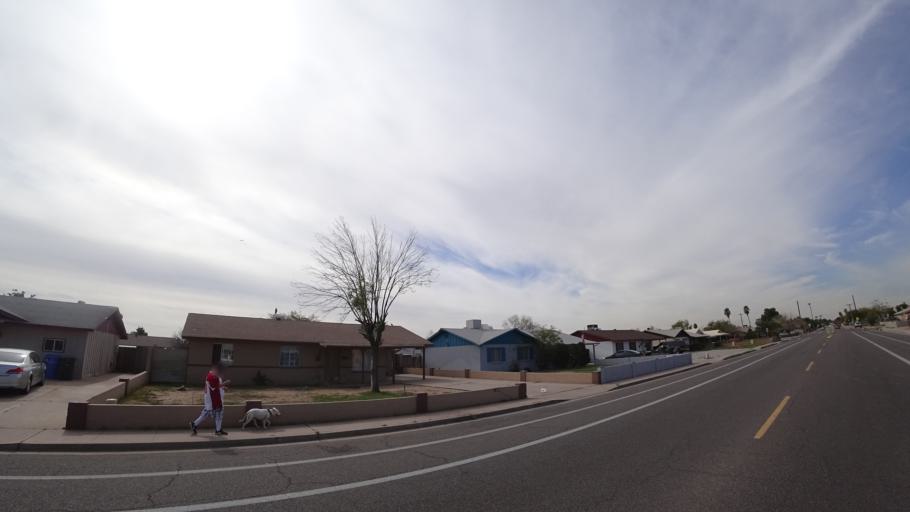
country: US
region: Arizona
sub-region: Maricopa County
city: Glendale
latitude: 33.4877
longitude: -112.1975
